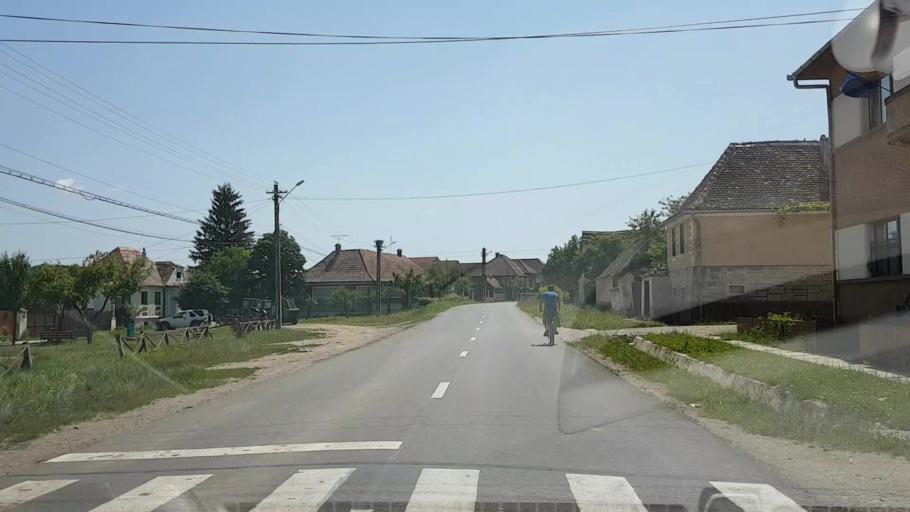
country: RO
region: Sibiu
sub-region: Comuna Merghindeal
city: Merghindeal
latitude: 45.9648
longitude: 24.7311
